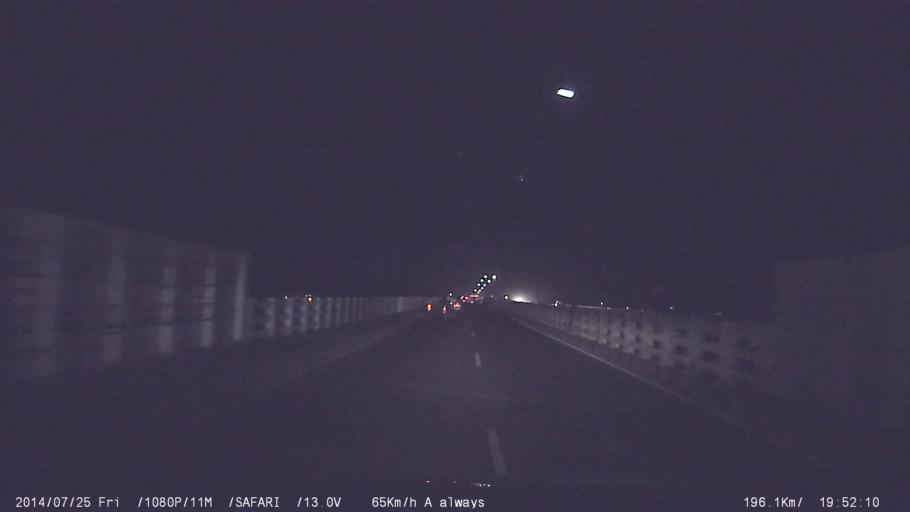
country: IN
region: Tamil Nadu
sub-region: Salem
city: Salem
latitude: 11.6618
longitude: 78.1219
